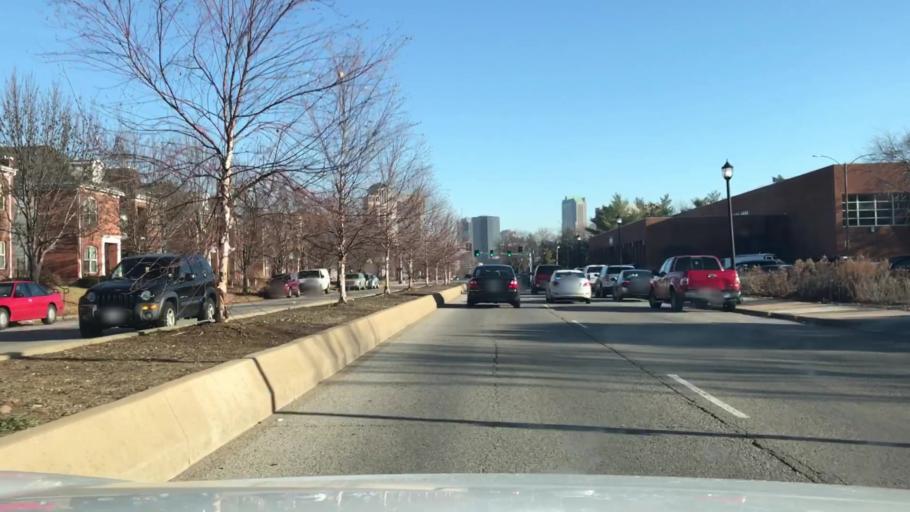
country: US
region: Missouri
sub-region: City of Saint Louis
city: St. Louis
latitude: 38.6136
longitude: -90.2053
